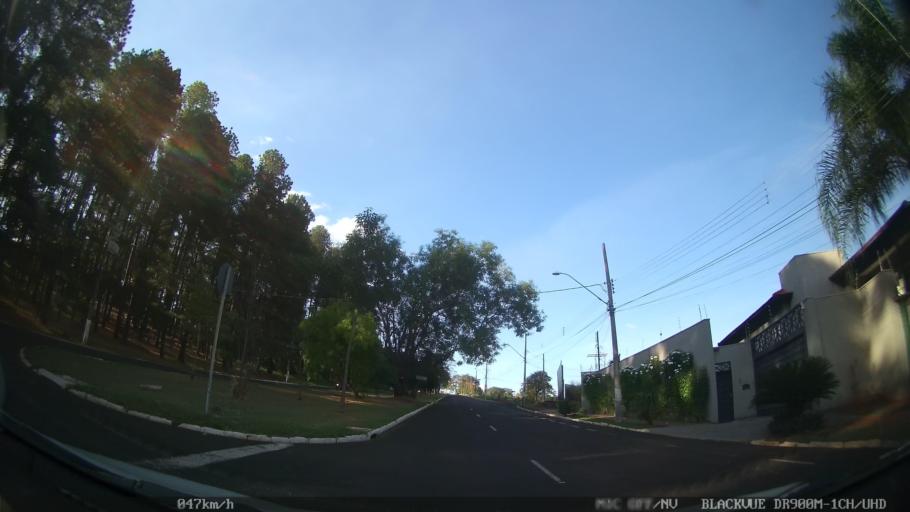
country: BR
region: Sao Paulo
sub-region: Ribeirao Preto
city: Ribeirao Preto
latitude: -21.2058
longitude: -47.7849
